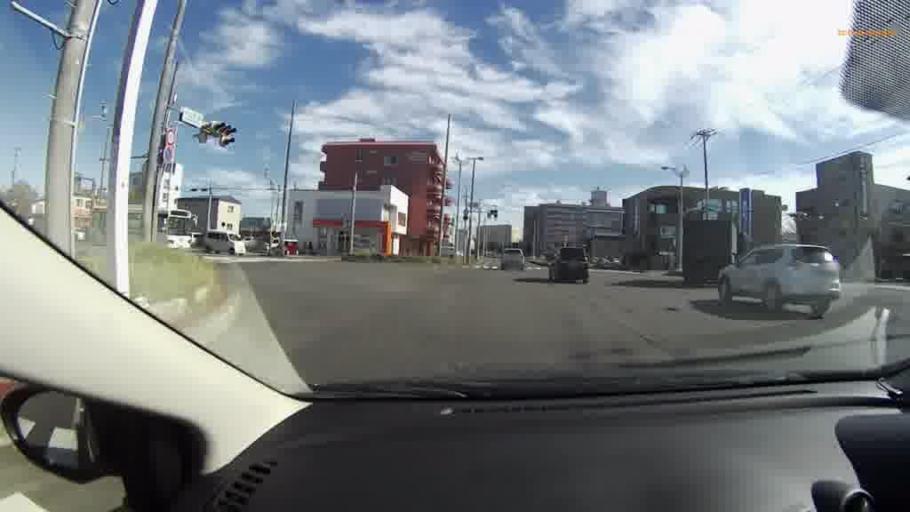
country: JP
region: Hokkaido
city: Kushiro
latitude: 42.9854
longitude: 144.3889
